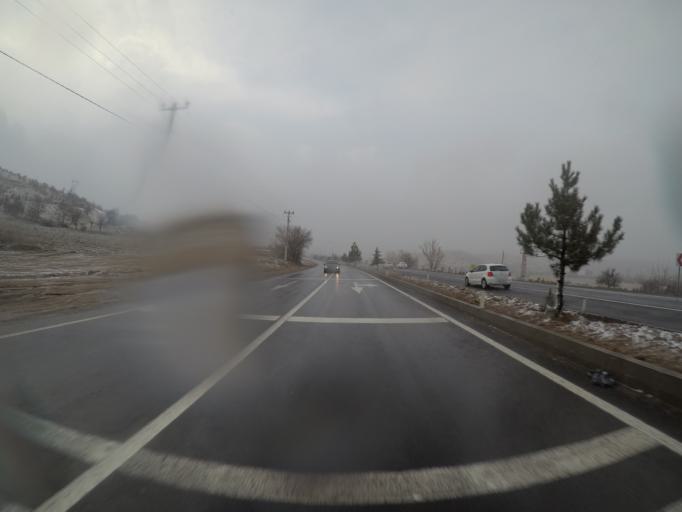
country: TR
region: Nevsehir
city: Nevsehir
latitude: 38.6307
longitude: 34.7625
